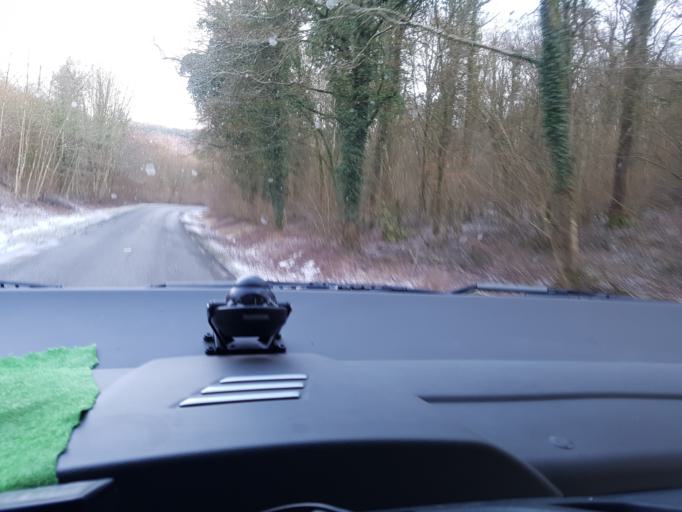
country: FR
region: Champagne-Ardenne
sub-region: Departement des Ardennes
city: Rimogne
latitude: 49.7144
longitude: 4.5304
